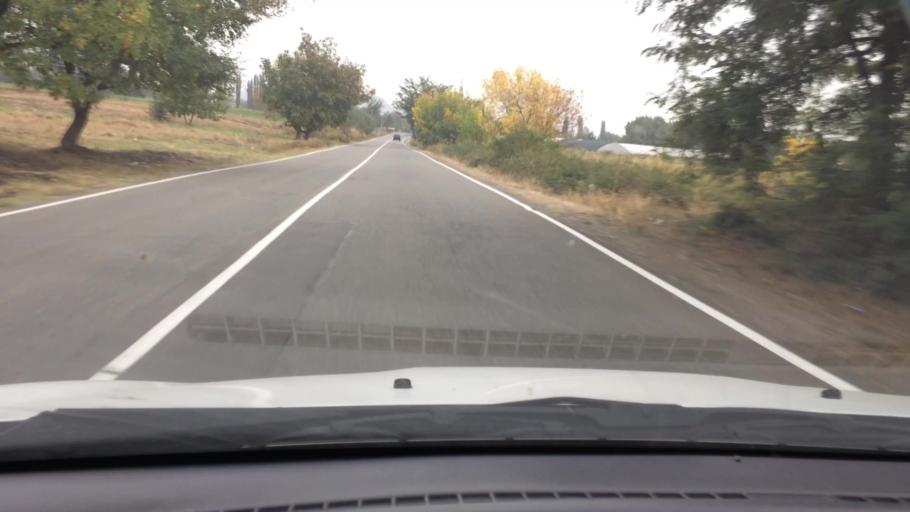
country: GE
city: Naghvarevi
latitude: 41.3180
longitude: 44.7947
